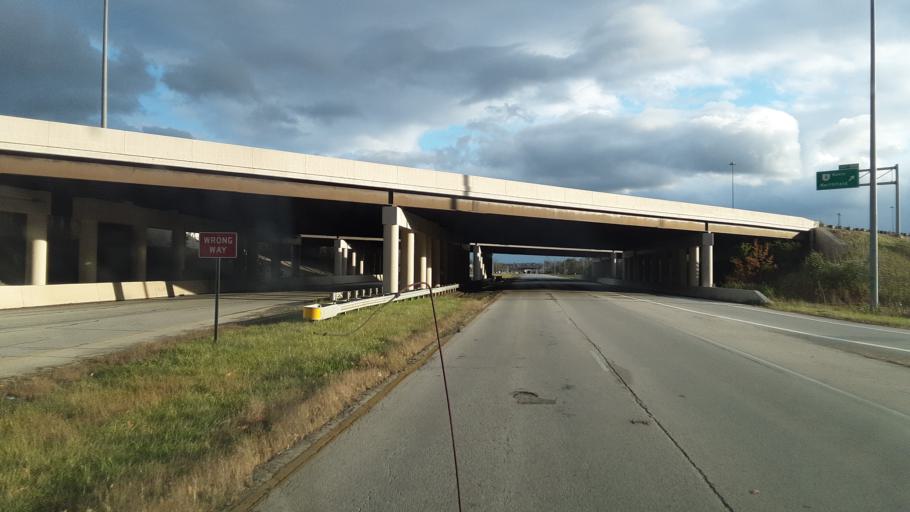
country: US
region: Ohio
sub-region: Summit County
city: Macedonia
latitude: 41.3046
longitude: -81.5180
